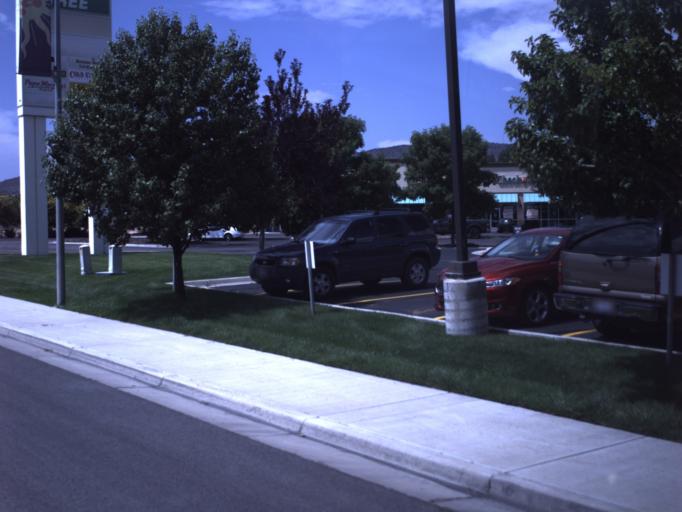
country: US
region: Utah
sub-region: Uintah County
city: Vernal
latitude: 40.4400
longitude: -109.5642
